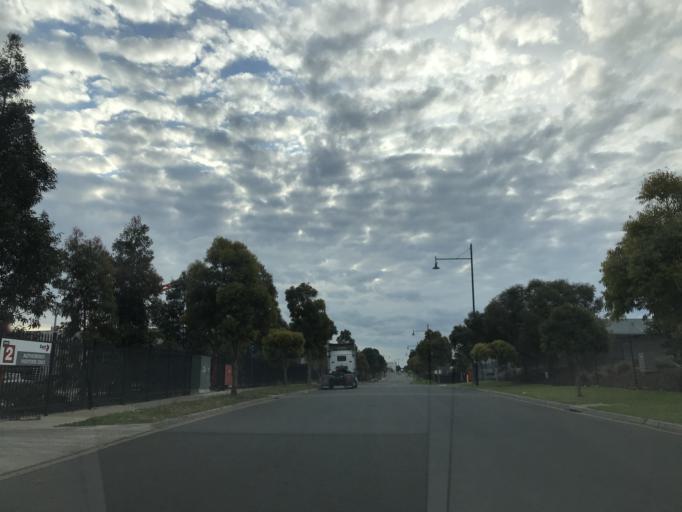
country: AU
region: Victoria
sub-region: Brimbank
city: Derrimut
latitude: -37.7999
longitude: 144.7580
